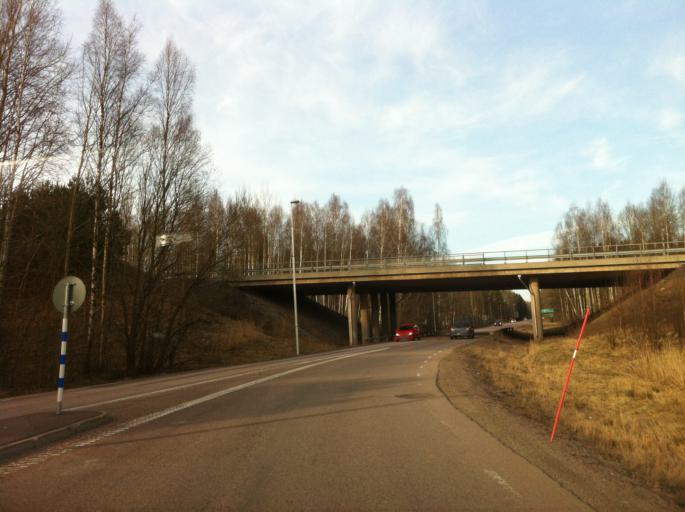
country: SE
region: Vaermland
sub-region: Kristinehamns Kommun
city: Kristinehamn
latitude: 59.3239
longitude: 14.1150
